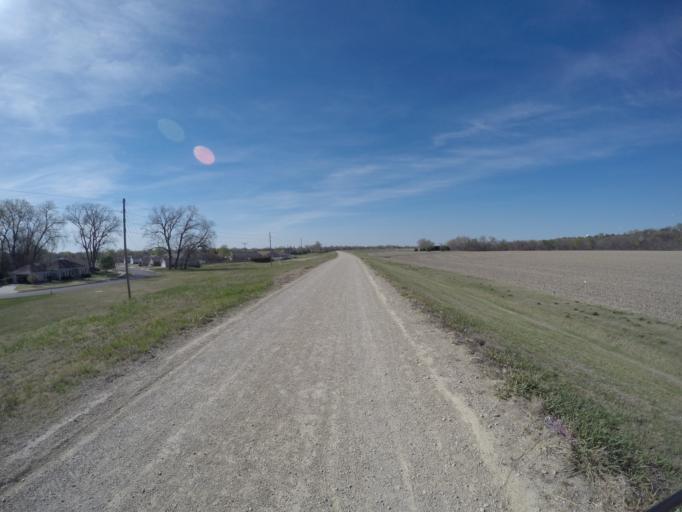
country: US
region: Kansas
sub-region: Saline County
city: Salina
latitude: 38.8200
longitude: -97.5840
